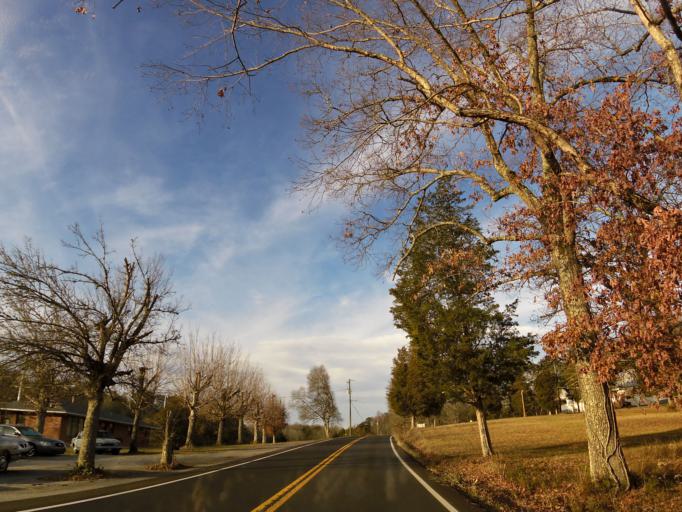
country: US
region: Tennessee
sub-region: Knox County
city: Mascot
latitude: 35.9864
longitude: -83.6958
